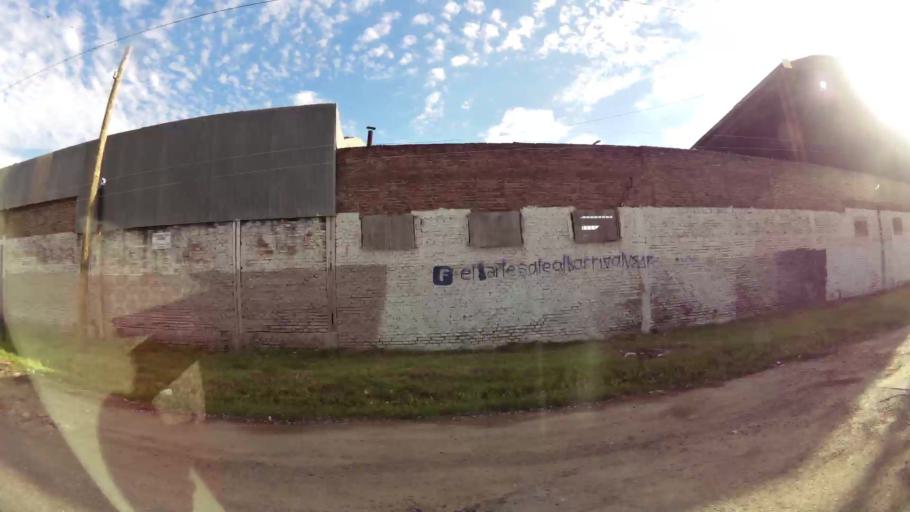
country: AR
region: Santa Fe
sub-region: Departamento de Rosario
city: Rosario
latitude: -32.9793
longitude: -60.6718
